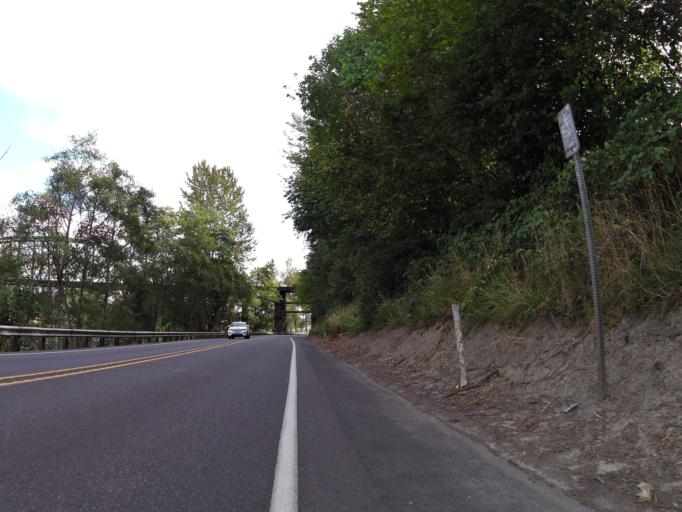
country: US
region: Washington
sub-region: Cowlitz County
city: West Side Highway
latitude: 46.1708
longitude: -122.9151
